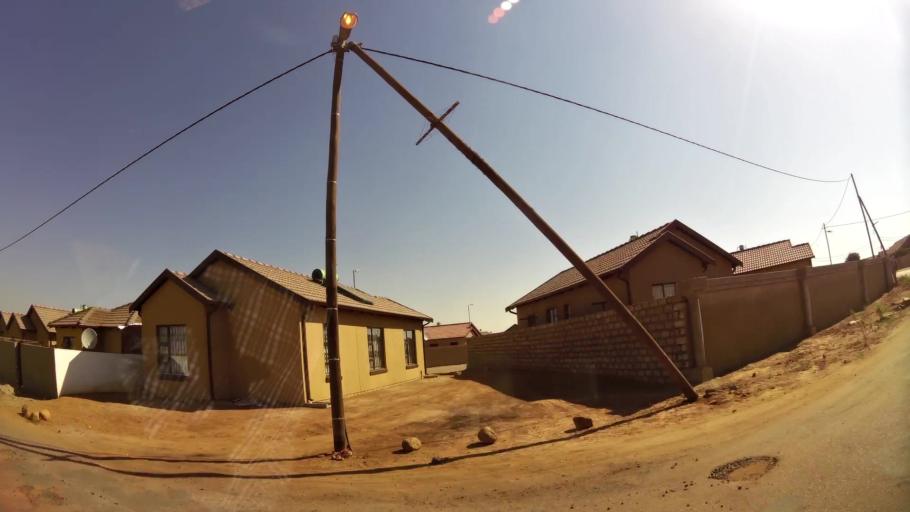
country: ZA
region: Gauteng
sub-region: City of Tshwane Metropolitan Municipality
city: Mabopane
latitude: -25.5638
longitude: 28.0847
